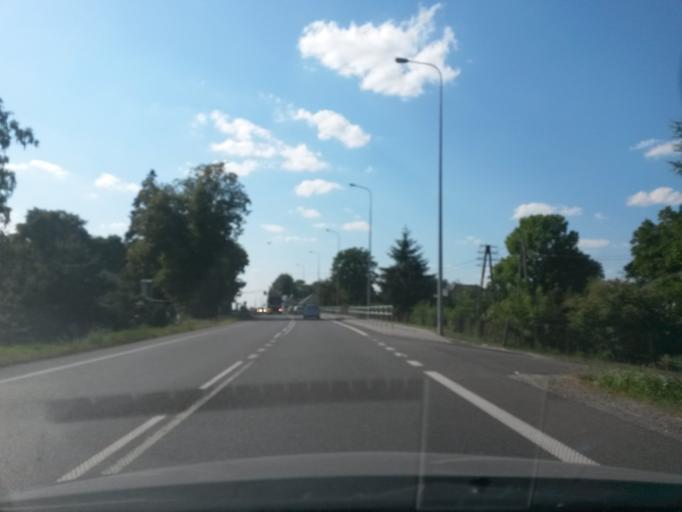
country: PL
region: Masovian Voivodeship
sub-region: Powiat plocki
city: Bulkowo
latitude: 52.6464
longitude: 20.0992
